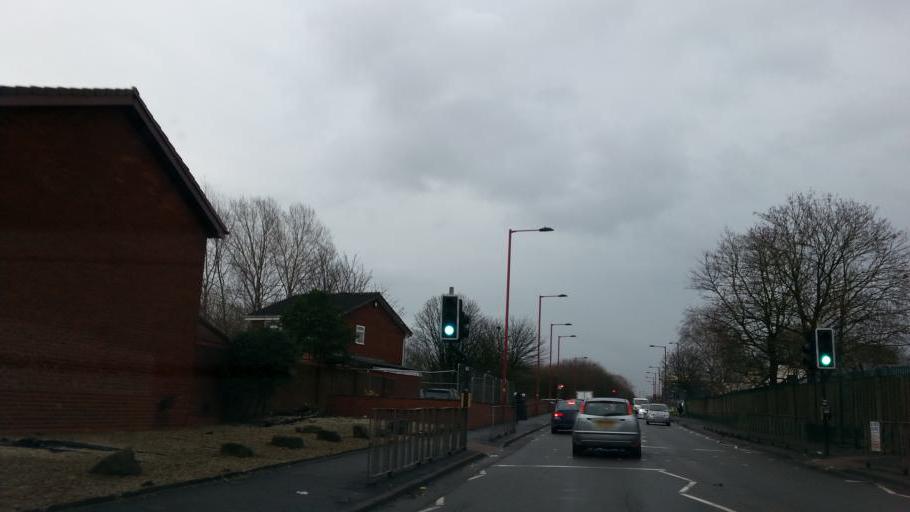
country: GB
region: England
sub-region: City and Borough of Birmingham
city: Hockley
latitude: 52.4892
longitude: -1.9396
